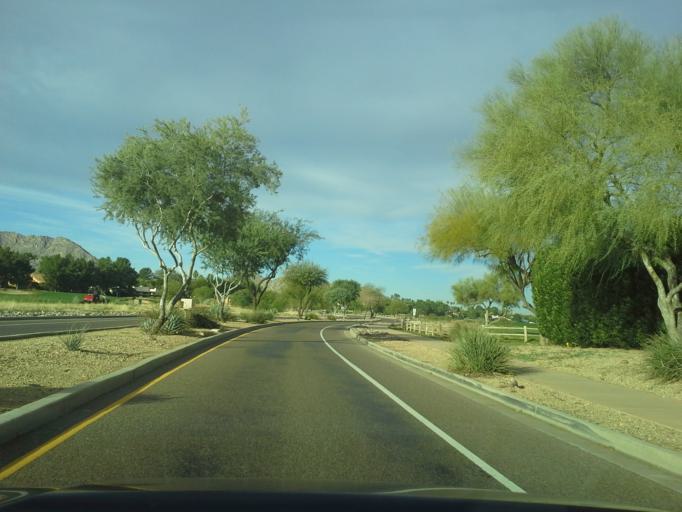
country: US
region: Arizona
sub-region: Maricopa County
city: Paradise Valley
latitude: 33.5679
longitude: -111.9516
